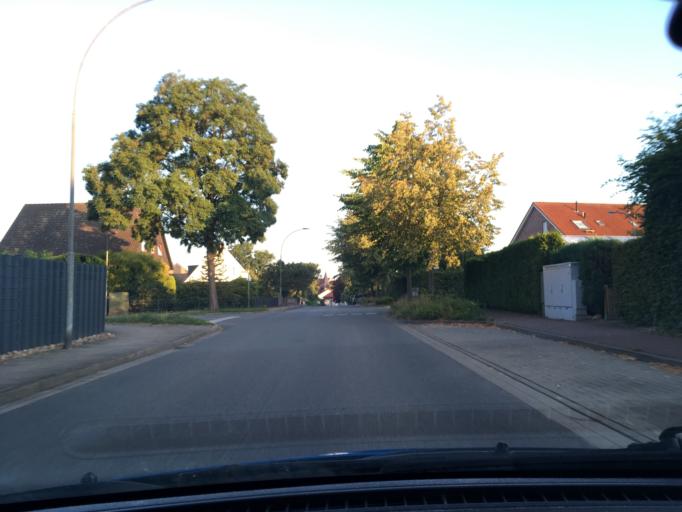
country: DE
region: Lower Saxony
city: Seevetal
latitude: 53.3853
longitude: 9.9882
